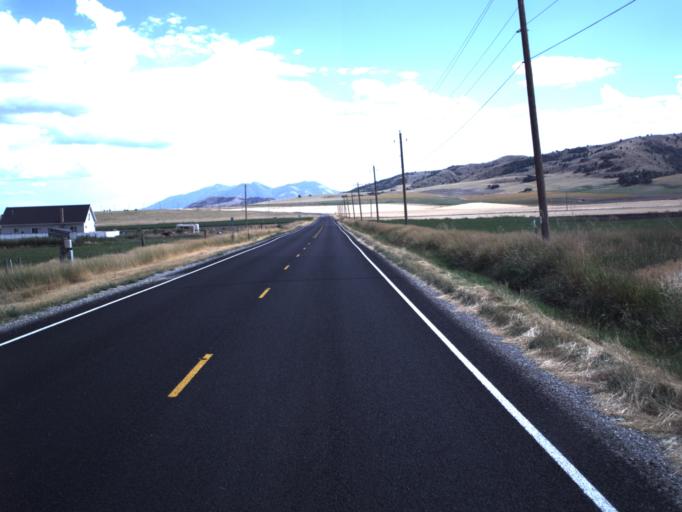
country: US
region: Utah
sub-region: Cache County
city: Benson
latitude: 41.9079
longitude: -112.0455
